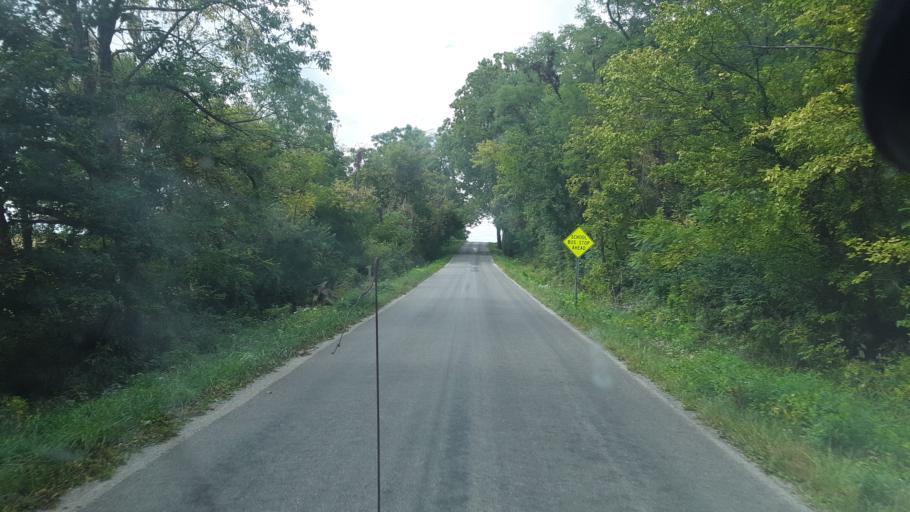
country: US
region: Ohio
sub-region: Delaware County
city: Sunbury
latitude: 40.2322
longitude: -82.7789
